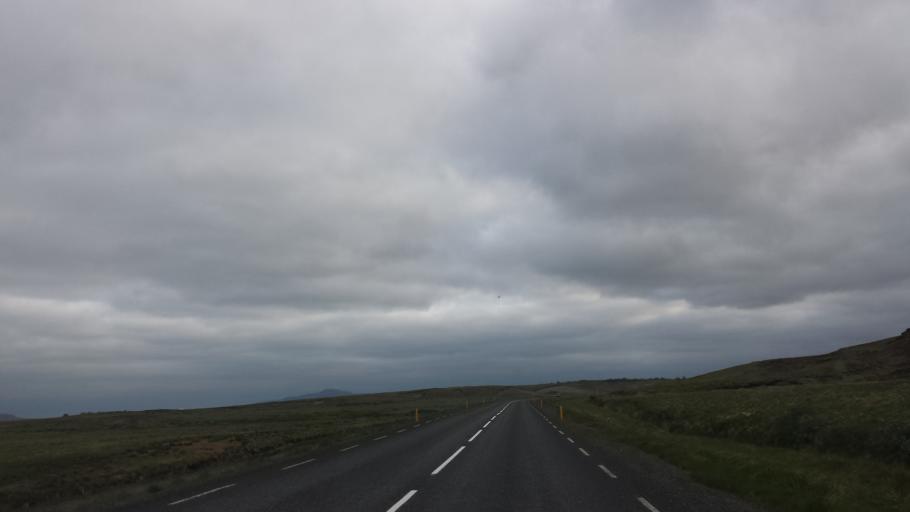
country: IS
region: South
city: Selfoss
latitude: 64.1321
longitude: -20.5812
